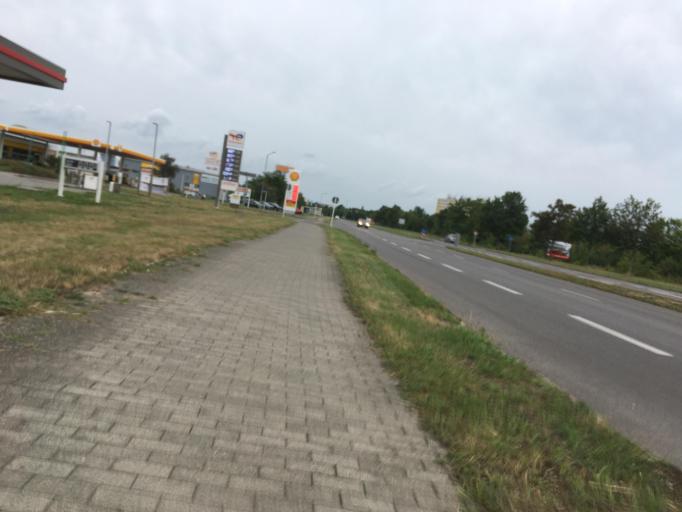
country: DE
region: Brandenburg
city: Schwedt (Oder)
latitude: 53.0713
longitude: 14.2538
